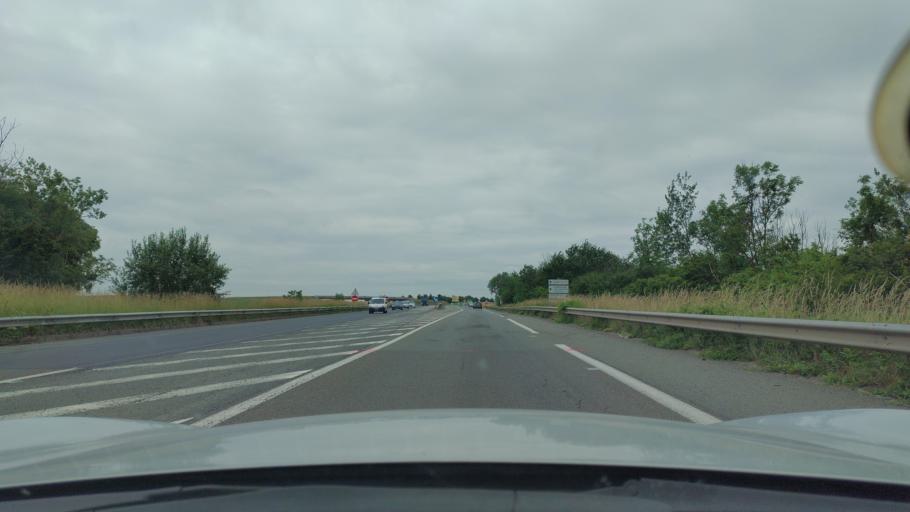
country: FR
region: Picardie
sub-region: Departement de l'Oise
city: Margny-les-Compiegne
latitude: 49.4383
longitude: 2.8276
